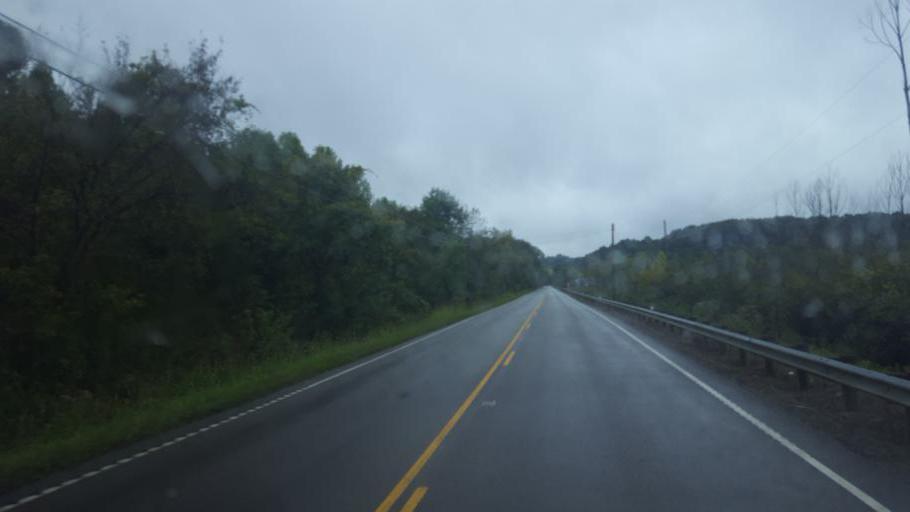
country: US
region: Ohio
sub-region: Jackson County
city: Oak Hill
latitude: 38.8063
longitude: -82.6919
